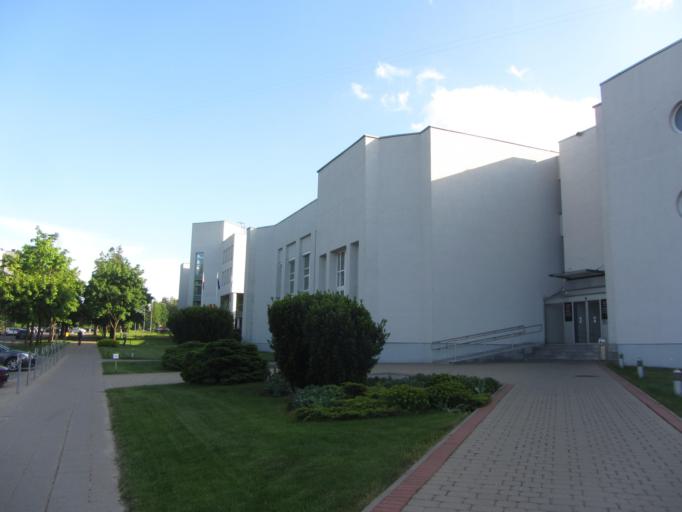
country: LT
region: Vilnius County
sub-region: Vilnius
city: Fabijoniskes
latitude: 54.7342
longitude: 25.2593
